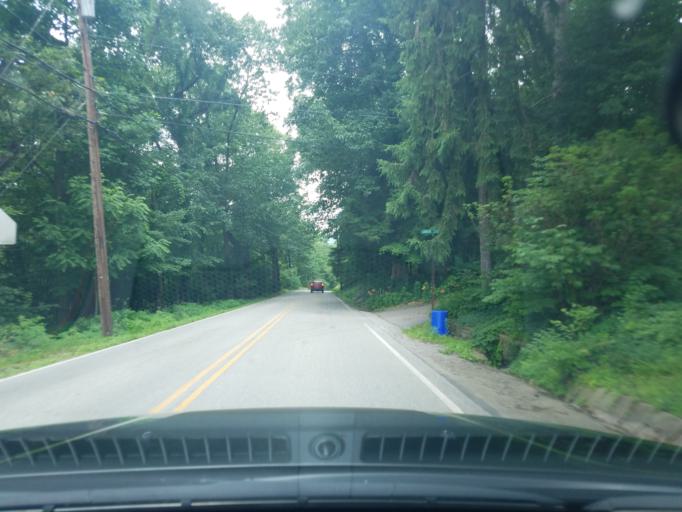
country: US
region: Pennsylvania
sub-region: Westmoreland County
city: Youngwood
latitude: 40.2214
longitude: -79.5768
